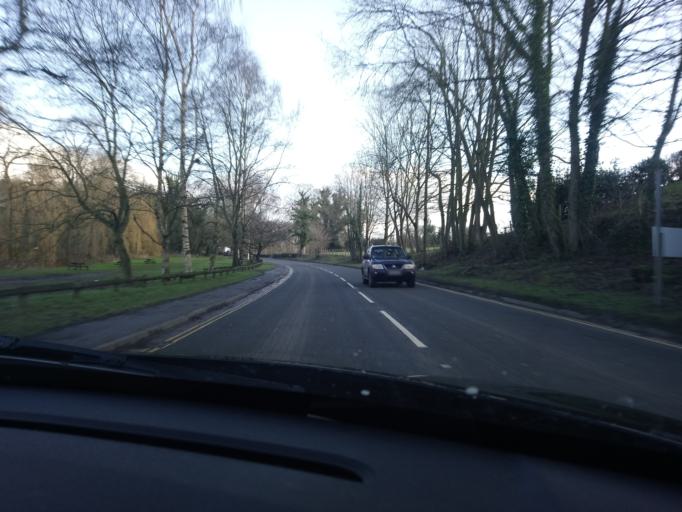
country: GB
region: England
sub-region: Shropshire
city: Ellesmere
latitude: 52.9031
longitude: -2.8812
